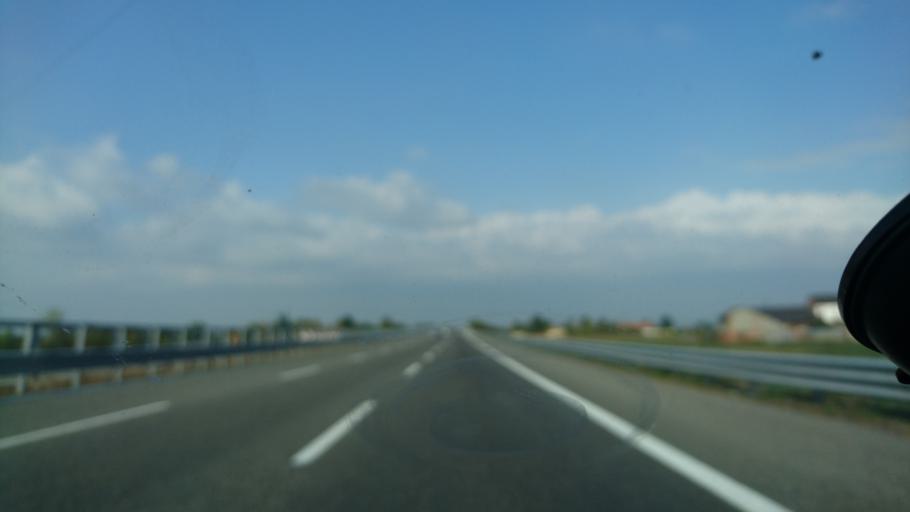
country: IT
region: Piedmont
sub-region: Provincia di Alessandria
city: Alessandria
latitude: 44.8914
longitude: 8.5691
